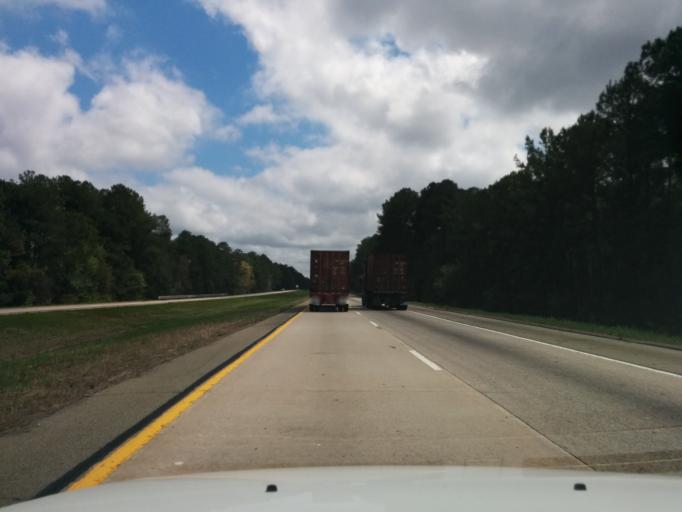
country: US
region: Georgia
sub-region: Bryan County
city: Pembroke
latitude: 32.1976
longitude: -81.4819
